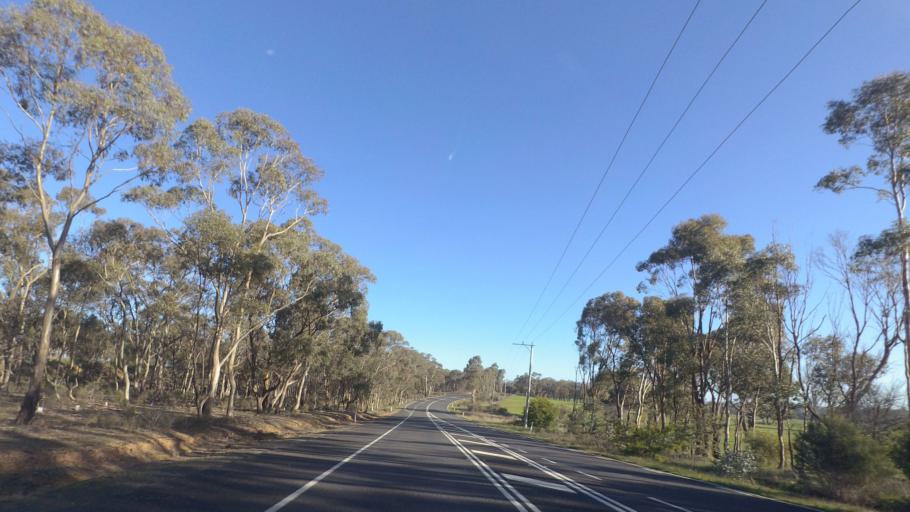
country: AU
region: Victoria
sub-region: Greater Bendigo
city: Kennington
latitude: -36.8573
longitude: 144.5057
